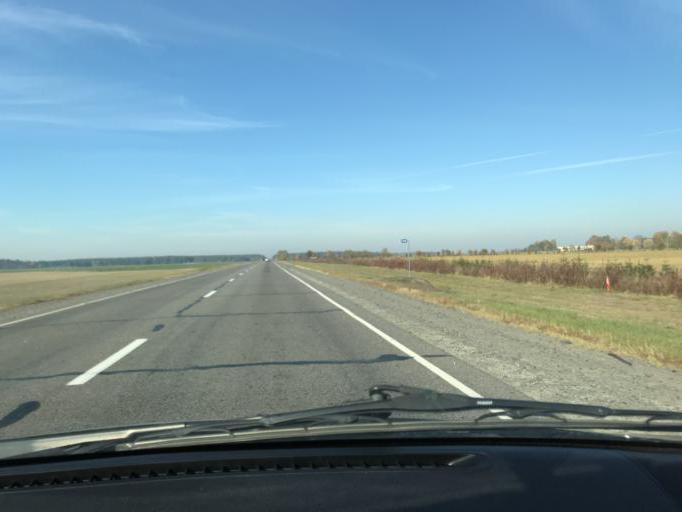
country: BY
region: Brest
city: Davyd-Haradok
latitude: 52.2503
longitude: 27.0665
